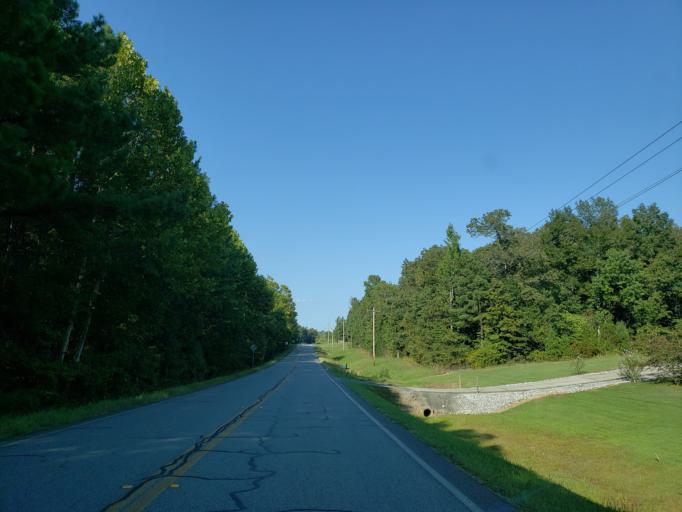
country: US
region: Georgia
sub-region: Whitfield County
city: Varnell
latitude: 34.9163
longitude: -84.8498
